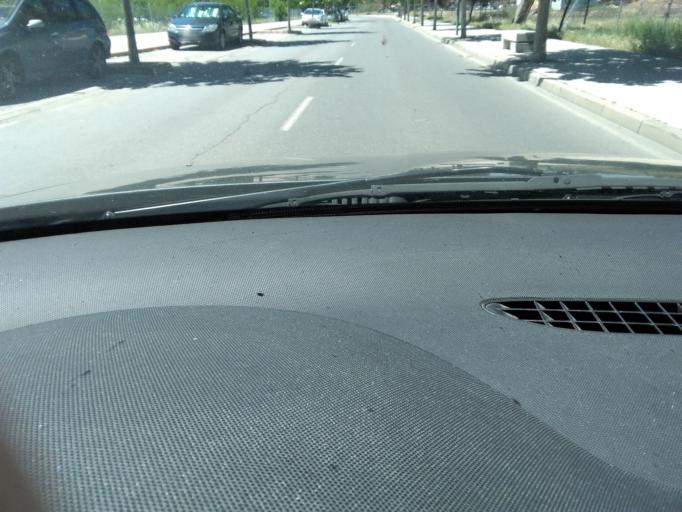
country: ES
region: Castille-La Mancha
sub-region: Province of Toledo
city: Toledo
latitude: 39.8661
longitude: -4.0388
